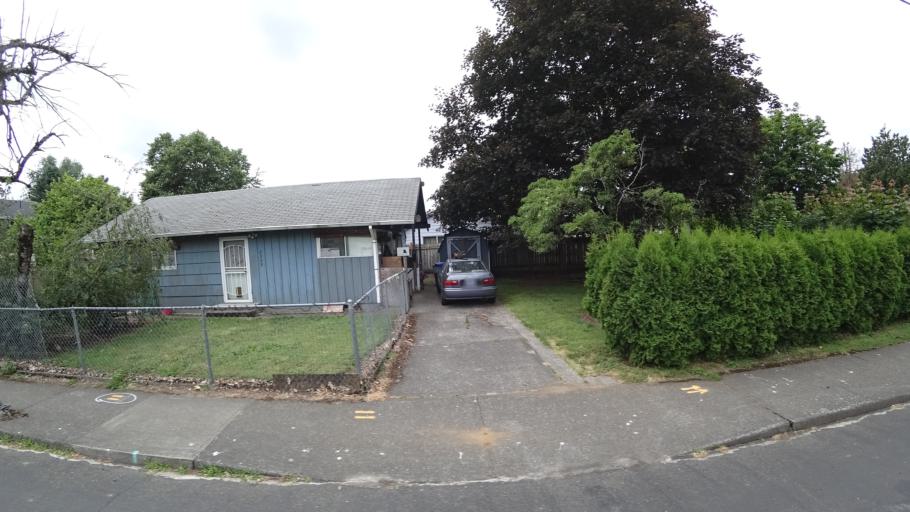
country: US
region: Oregon
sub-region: Multnomah County
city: Lents
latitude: 45.4842
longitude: -122.5609
